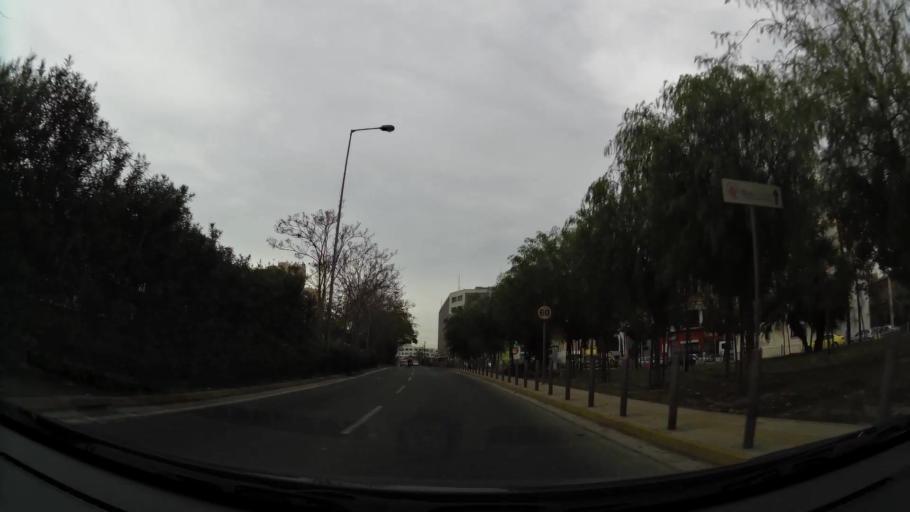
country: GR
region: Attica
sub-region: Nomos Attikis
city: Piraeus
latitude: 37.9484
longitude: 23.6551
